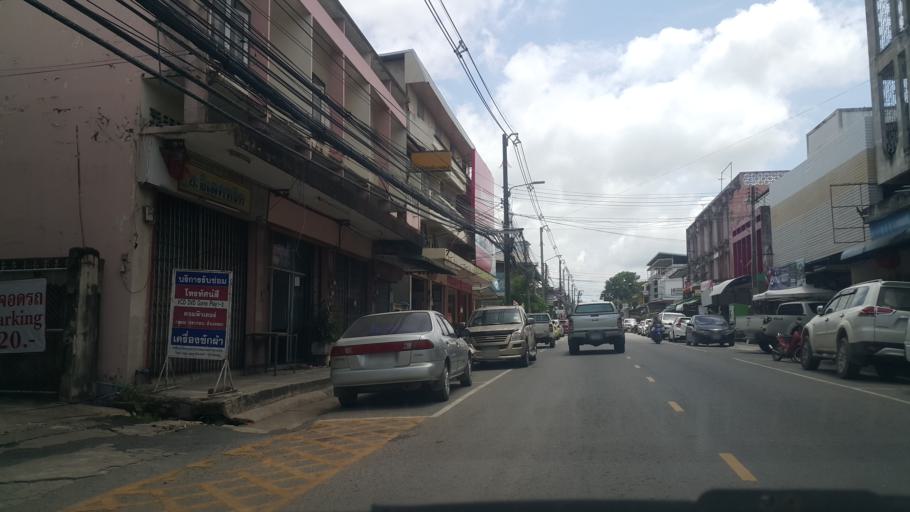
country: TH
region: Rayong
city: Ban Chang
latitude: 12.7261
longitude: 101.0536
